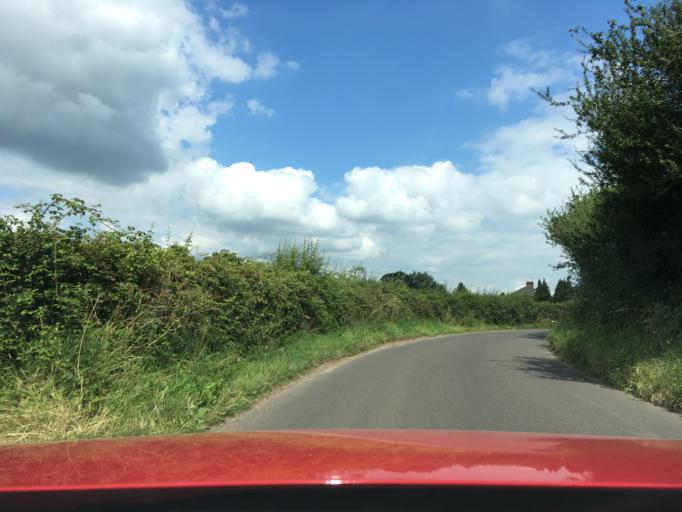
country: GB
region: England
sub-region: Gloucestershire
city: Gloucester
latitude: 51.8972
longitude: -2.2528
